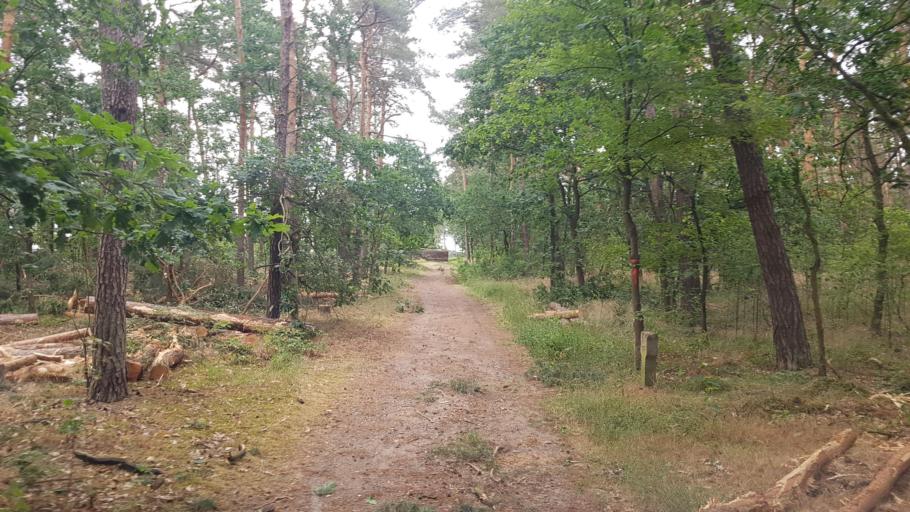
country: DE
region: Saxony-Anhalt
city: Abtsdorf
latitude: 51.8868
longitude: 12.7153
